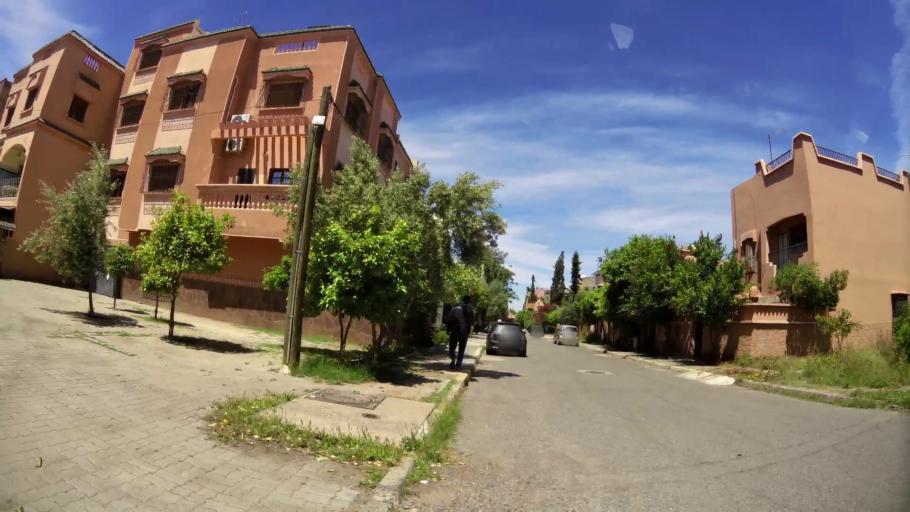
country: MA
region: Marrakech-Tensift-Al Haouz
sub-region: Marrakech
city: Marrakesh
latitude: 31.6415
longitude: -8.0551
